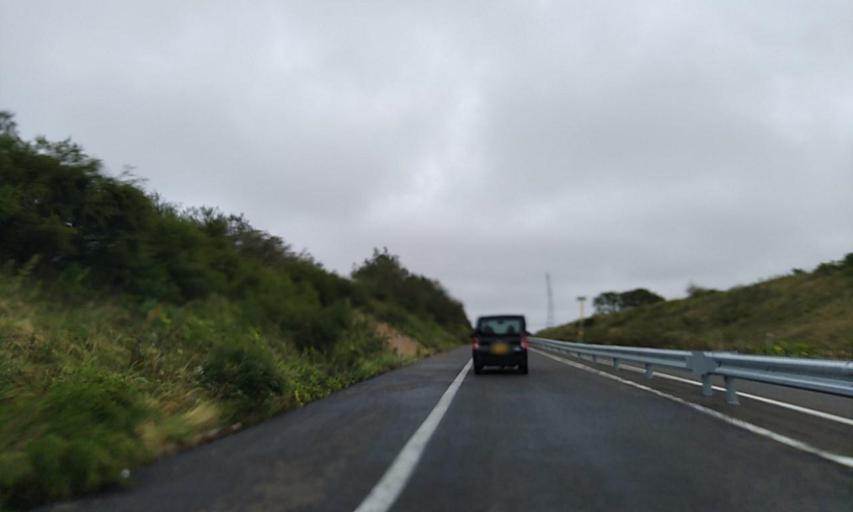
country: JP
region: Hokkaido
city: Nemuro
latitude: 43.2987
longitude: 145.5264
